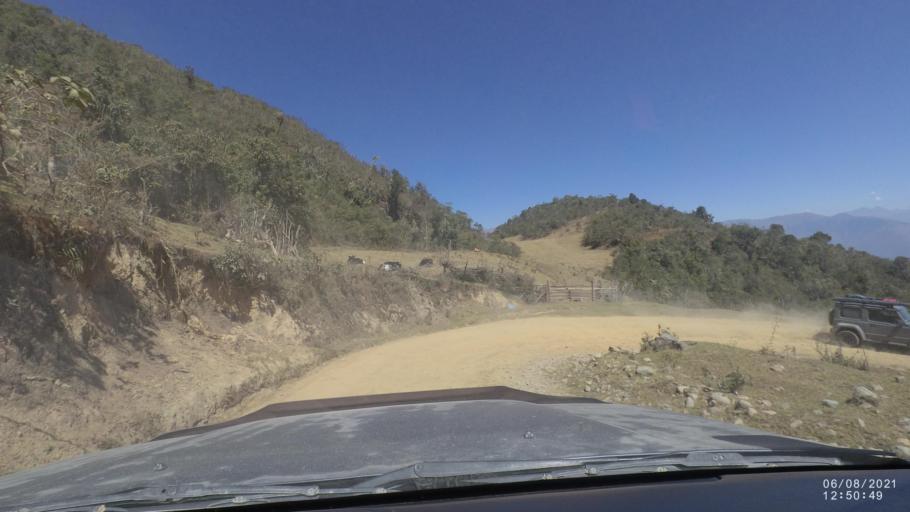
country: BO
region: Cochabamba
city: Colchani
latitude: -16.7615
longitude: -66.6791
